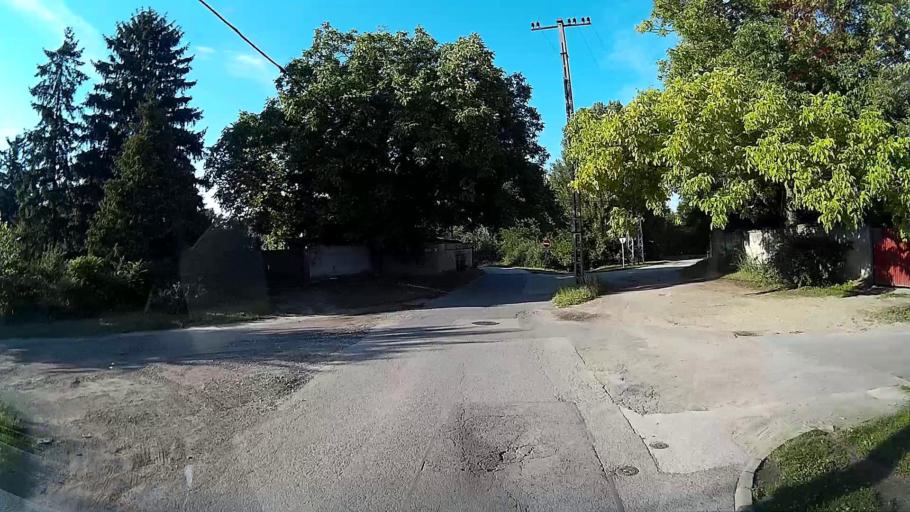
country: HU
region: Pest
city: Szentendre
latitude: 47.6869
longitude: 19.1024
